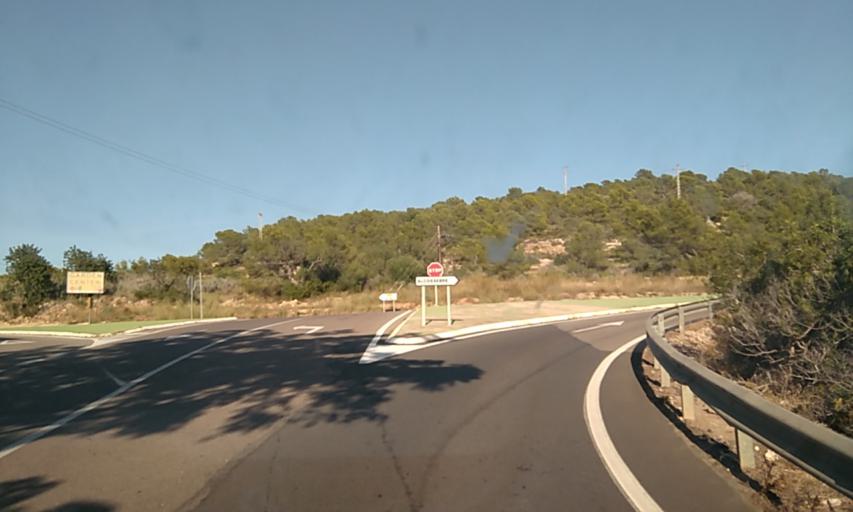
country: ES
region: Valencia
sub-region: Provincia de Castello
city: Alcoceber
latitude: 40.2501
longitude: 0.2472
